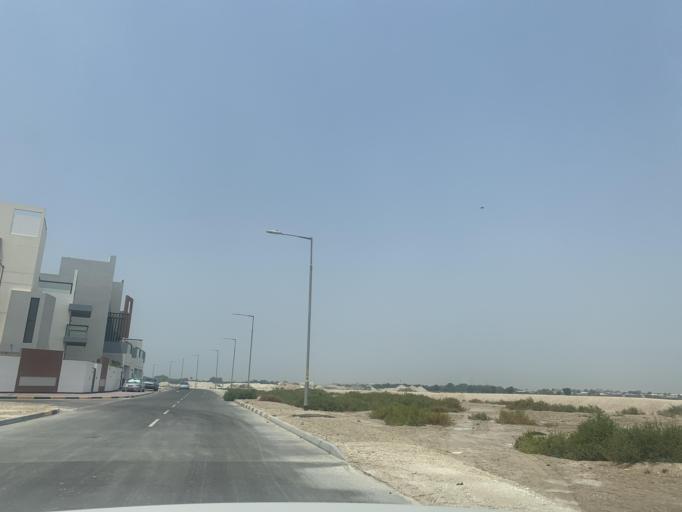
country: BH
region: Central Governorate
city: Madinat Hamad
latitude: 26.1327
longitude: 50.4700
